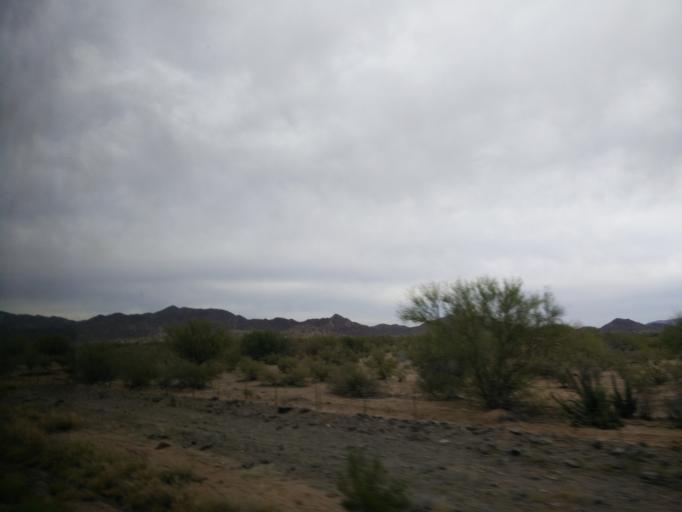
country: MX
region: Sonora
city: Hermosillo
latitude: 28.9260
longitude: -110.9528
